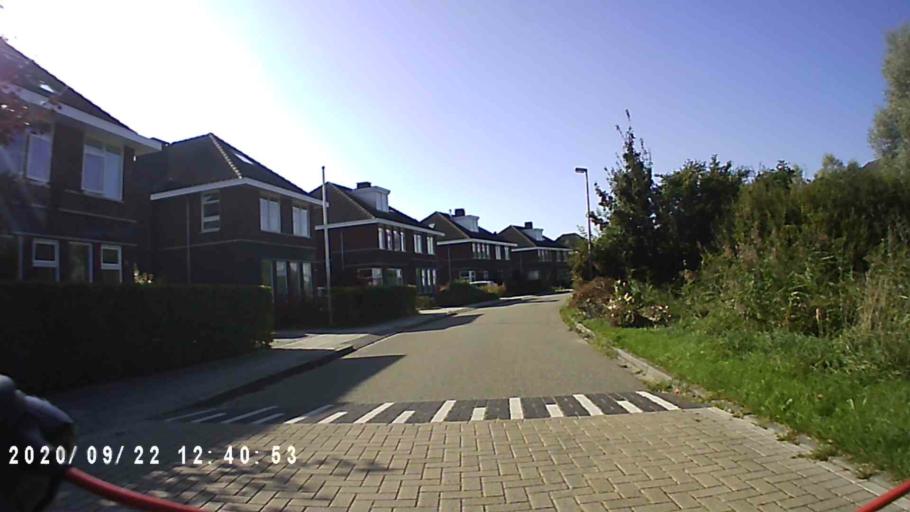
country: NL
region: Groningen
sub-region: Gemeente Zuidhorn
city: Noordhorn
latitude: 53.2500
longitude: 6.3869
